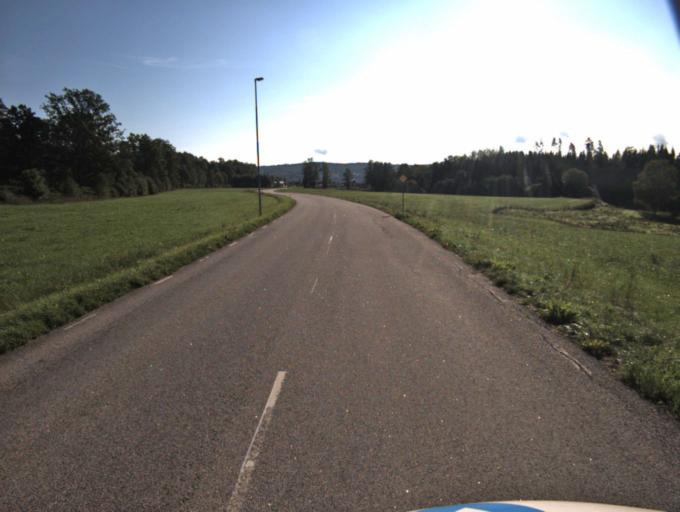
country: SE
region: Vaestra Goetaland
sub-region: Ulricehamns Kommun
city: Ulricehamn
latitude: 57.7989
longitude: 13.3822
